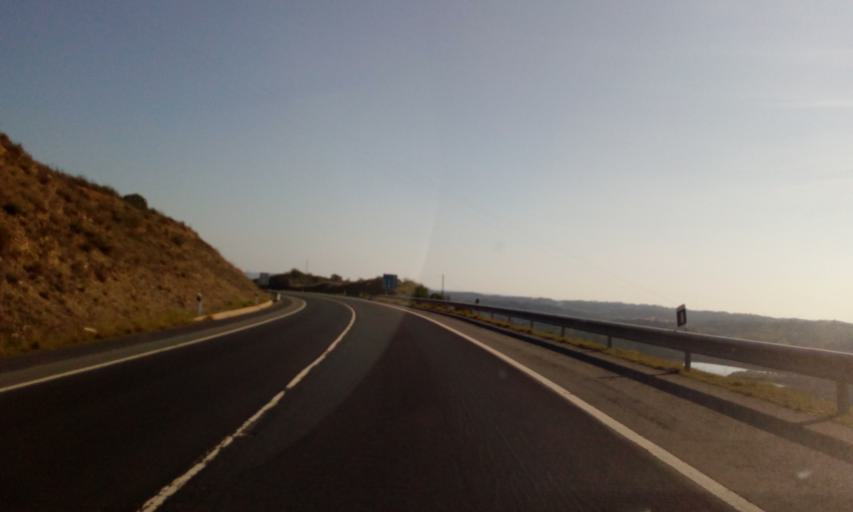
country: PT
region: Faro
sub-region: Castro Marim
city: Castro Marim
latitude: 37.2606
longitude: -7.4928
